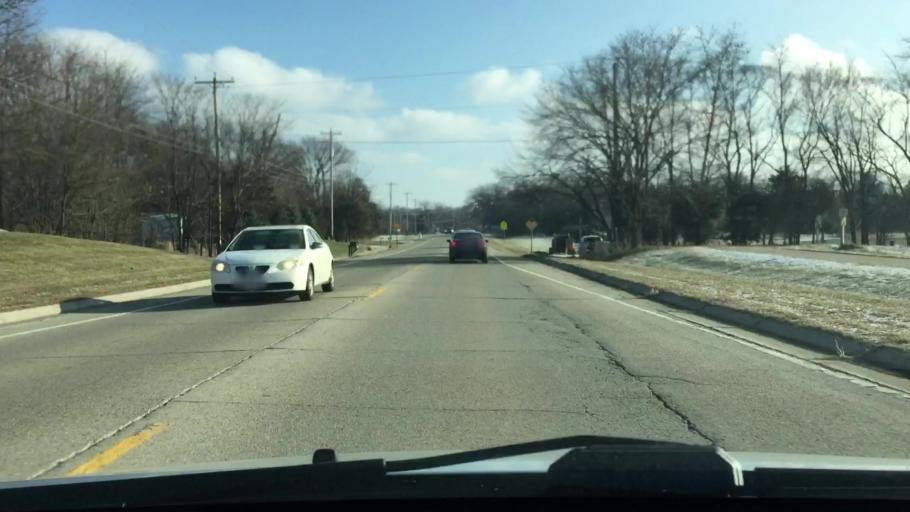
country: US
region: Wisconsin
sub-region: Waukesha County
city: Dousman
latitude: 43.0215
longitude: -88.4481
